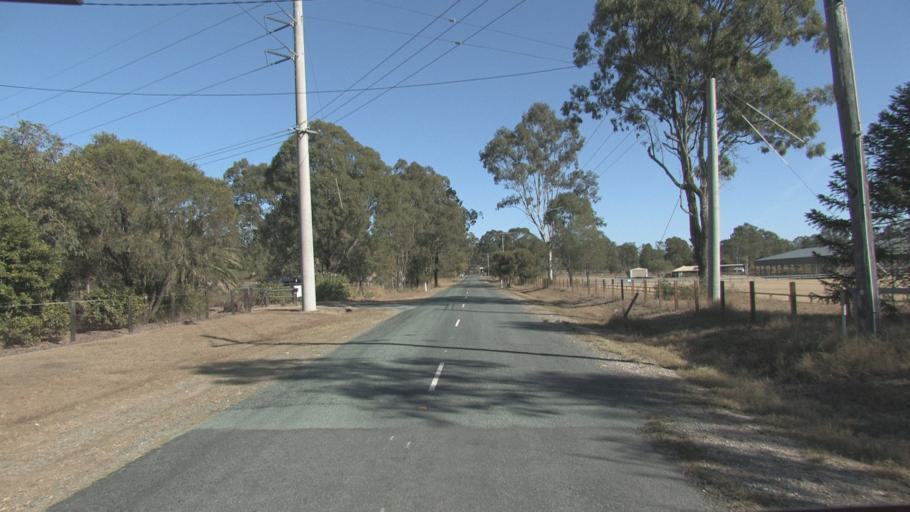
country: AU
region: Queensland
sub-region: Logan
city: Cedar Vale
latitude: -27.8409
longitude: 153.0301
